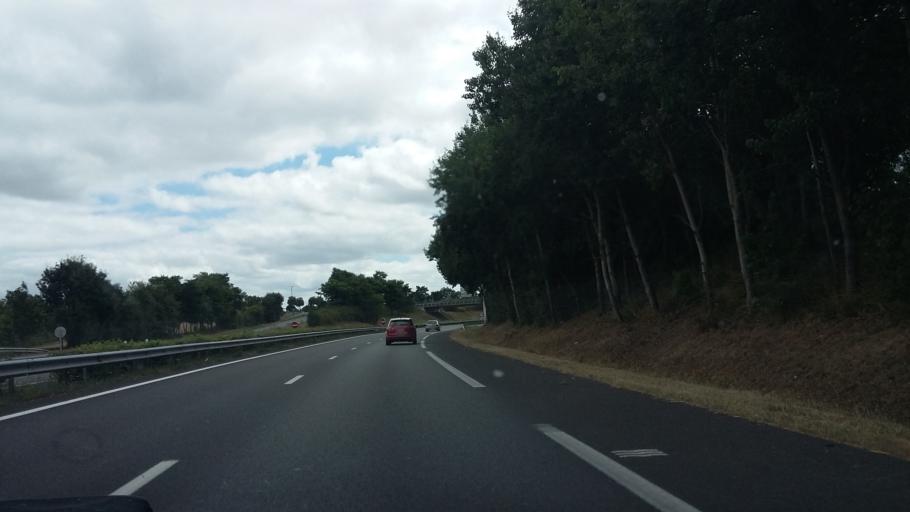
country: FR
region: Pays de la Loire
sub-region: Departement de la Vendee
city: Challans
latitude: 46.8540
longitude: -1.8521
